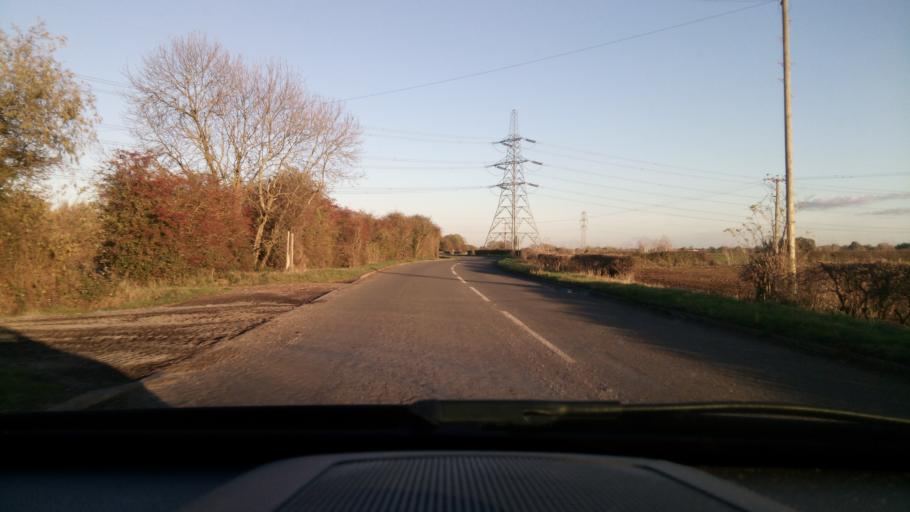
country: GB
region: England
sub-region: Peterborough
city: Ufford
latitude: 52.6434
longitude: -0.3694
